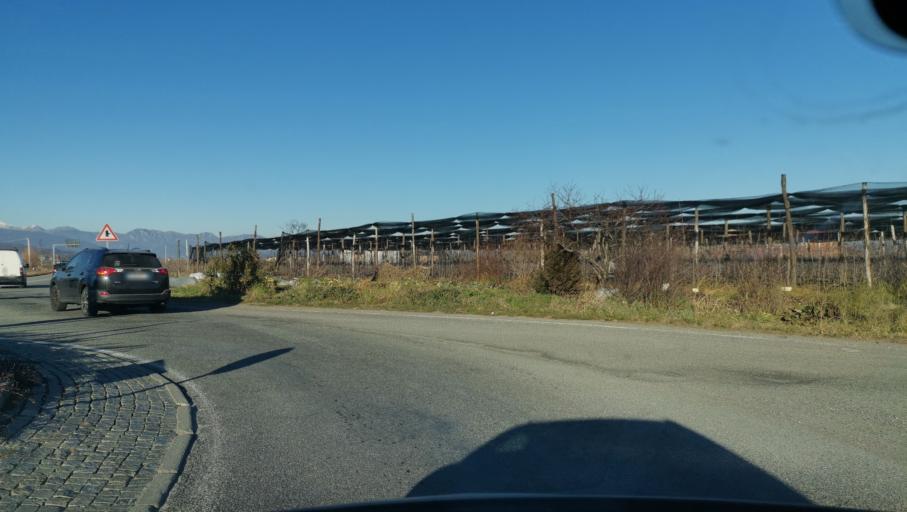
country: IT
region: Piedmont
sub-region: Provincia di Torino
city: Bibiana
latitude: 44.7963
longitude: 7.2965
